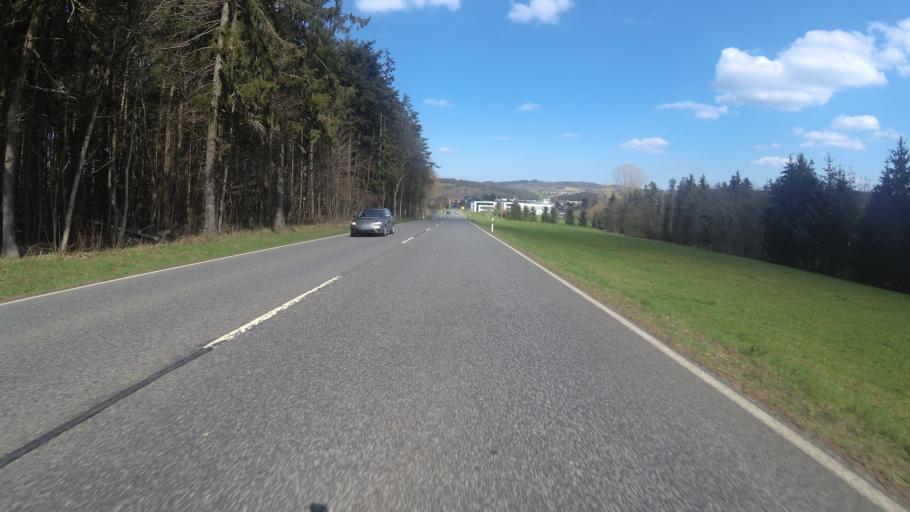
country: DE
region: Rheinland-Pfalz
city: Kelberg
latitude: 50.2816
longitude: 6.9080
